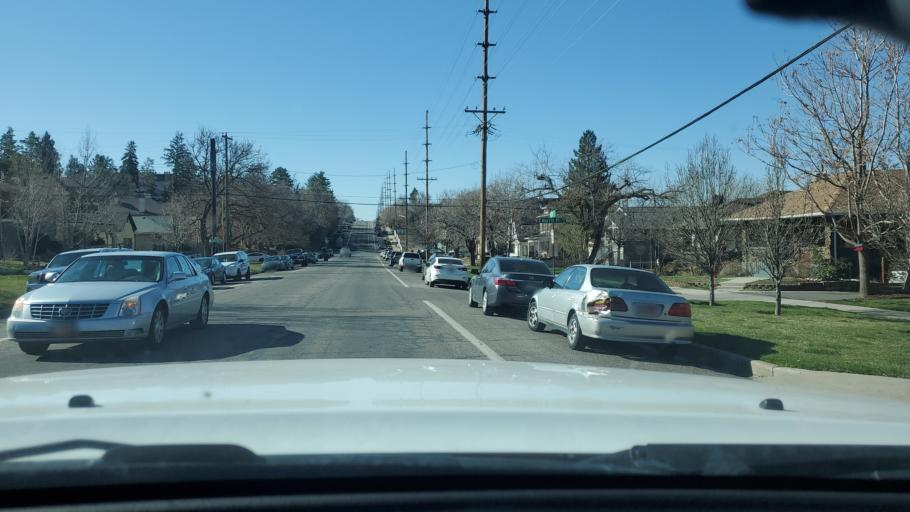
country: US
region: Utah
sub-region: Salt Lake County
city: Salt Lake City
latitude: 40.7644
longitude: -111.8597
